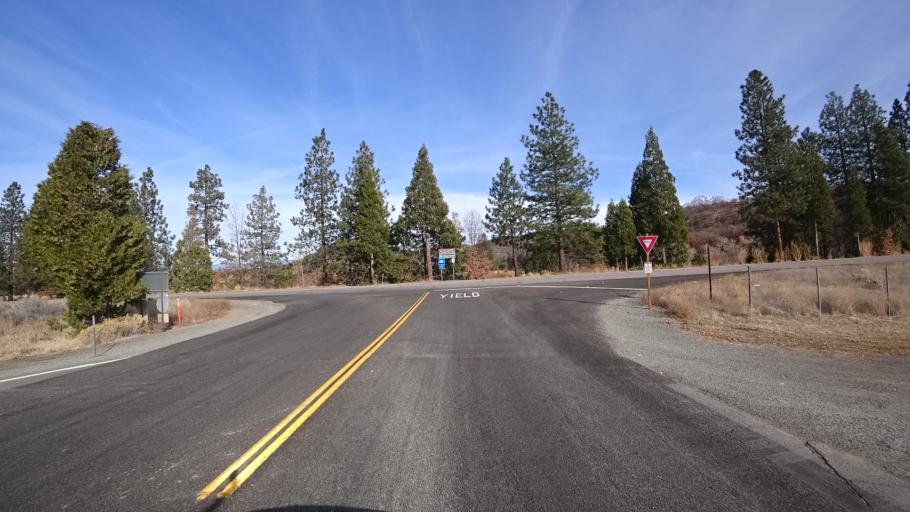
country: US
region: California
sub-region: Siskiyou County
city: Weed
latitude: 41.4424
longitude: -122.4342
